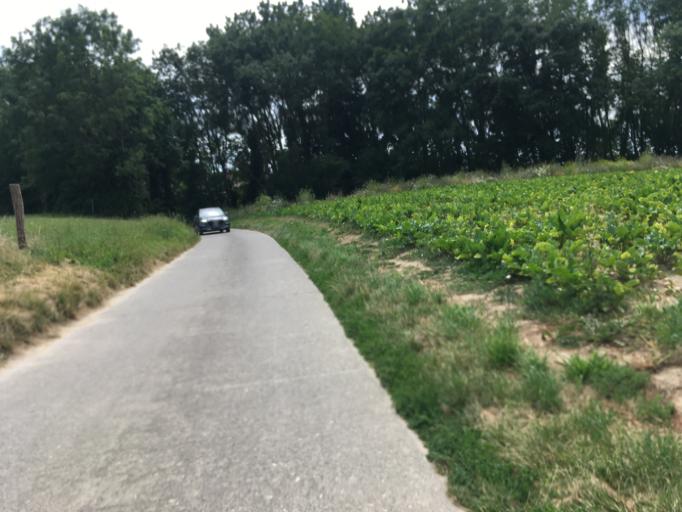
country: CH
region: Fribourg
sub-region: Broye District
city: Estavayer-le-Lac
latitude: 46.8785
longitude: 6.8902
